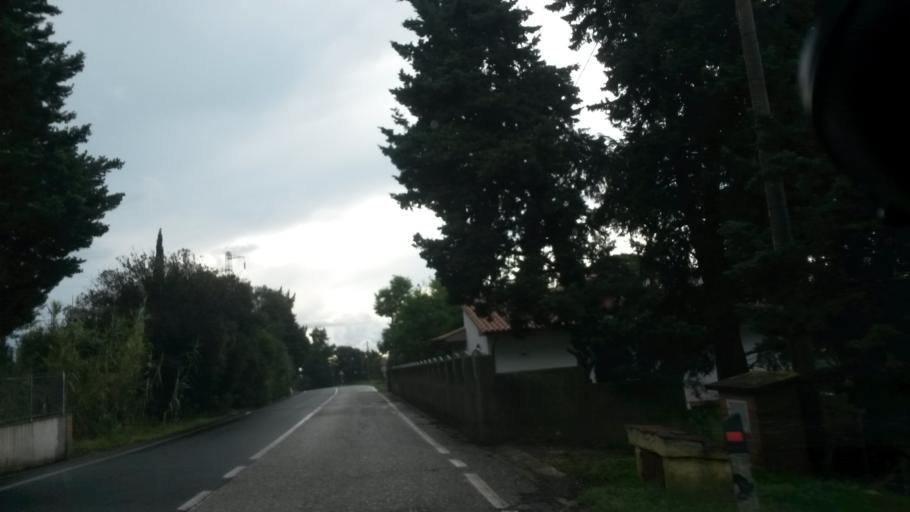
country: IT
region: Tuscany
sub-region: Provincia di Livorno
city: Rosignano Marittimo
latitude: 43.4134
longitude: 10.4508
